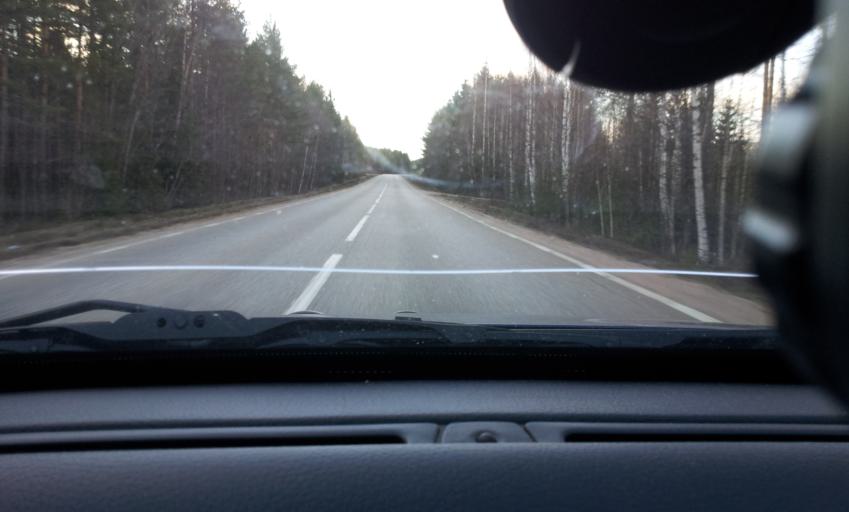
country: SE
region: Vaesternorrland
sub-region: Ange Kommun
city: Ange
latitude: 62.0801
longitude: 15.0986
